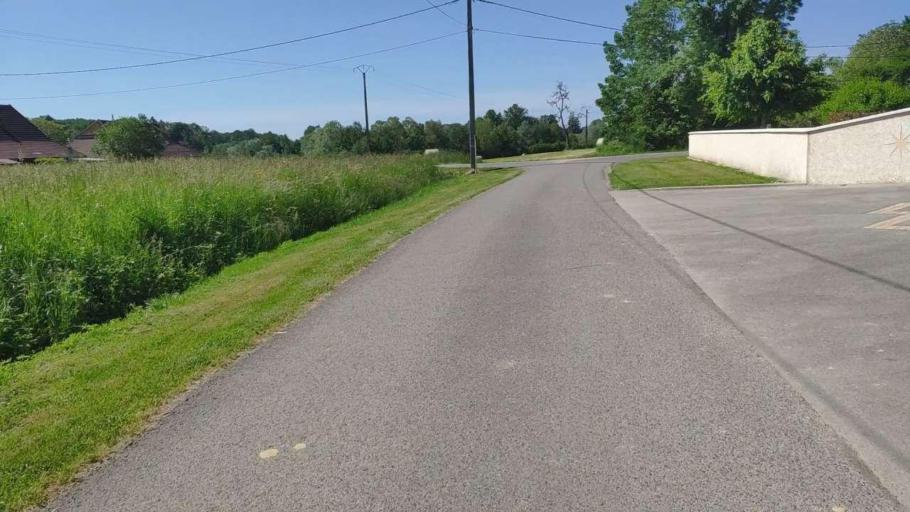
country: FR
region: Franche-Comte
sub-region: Departement du Jura
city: Bletterans
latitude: 46.7812
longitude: 5.4231
